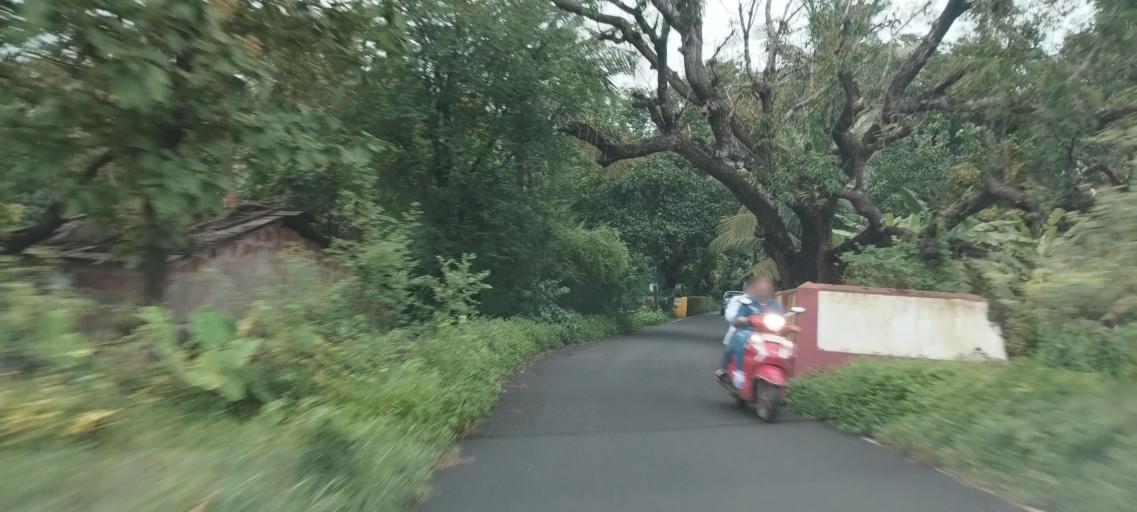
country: IN
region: Goa
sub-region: North Goa
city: Jua
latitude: 15.5199
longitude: 73.8961
